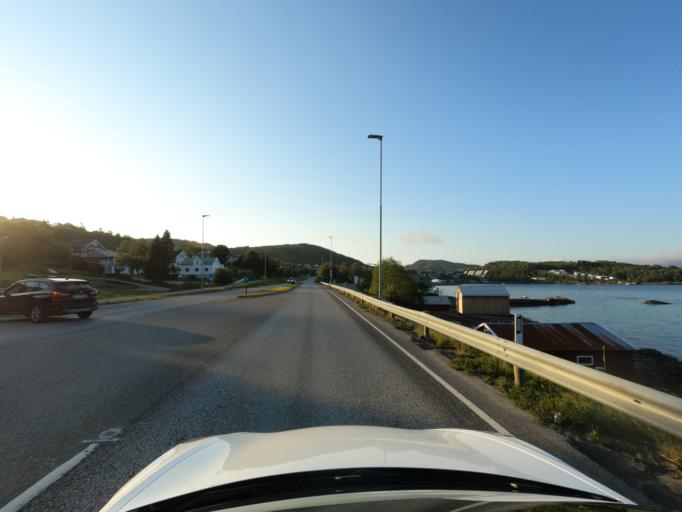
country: NO
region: Troms
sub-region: Harstad
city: Harstad
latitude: 68.7663
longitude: 16.5598
